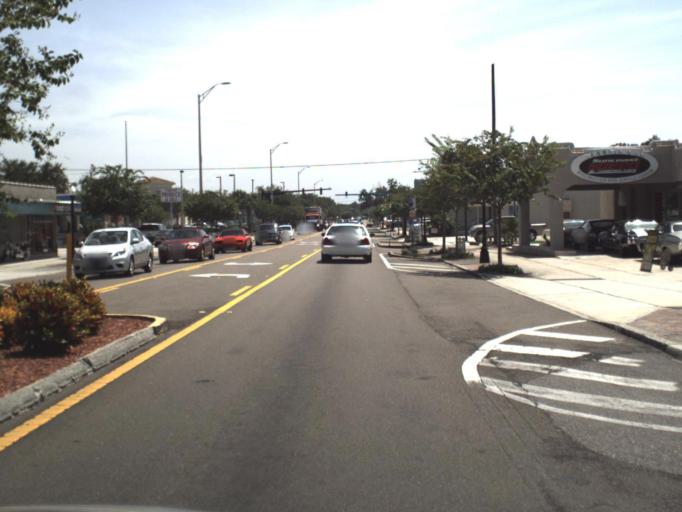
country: US
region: Florida
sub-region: Pinellas County
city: Tarpon Springs
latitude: 28.1428
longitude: -82.7567
